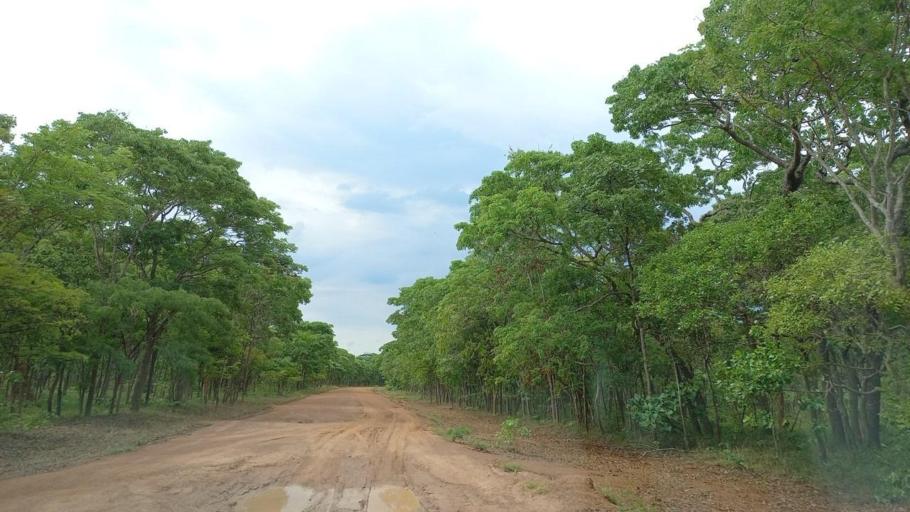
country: ZM
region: North-Western
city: Kalengwa
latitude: -13.3903
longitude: 25.0703
